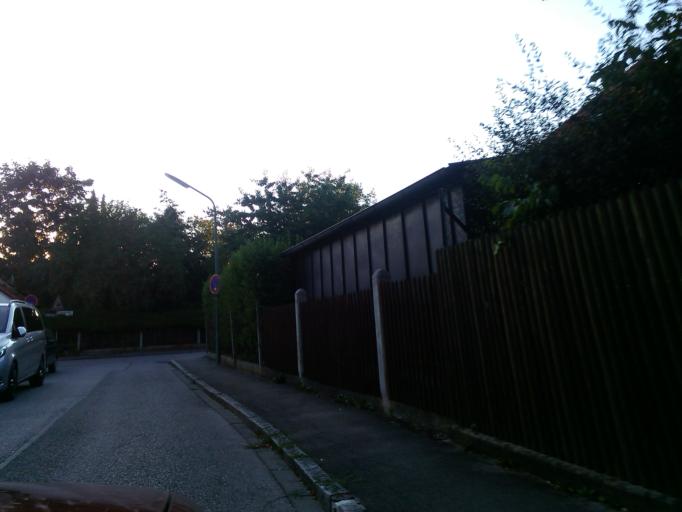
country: DE
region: Bavaria
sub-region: Upper Bavaria
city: Planegg
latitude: 48.1027
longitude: 11.4181
